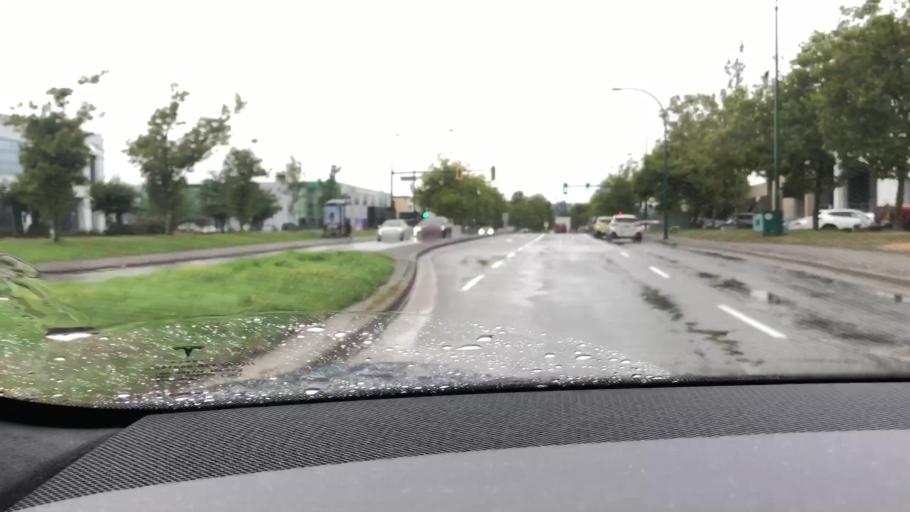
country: CA
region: British Columbia
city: Port Moody
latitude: 49.2292
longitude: -122.8516
